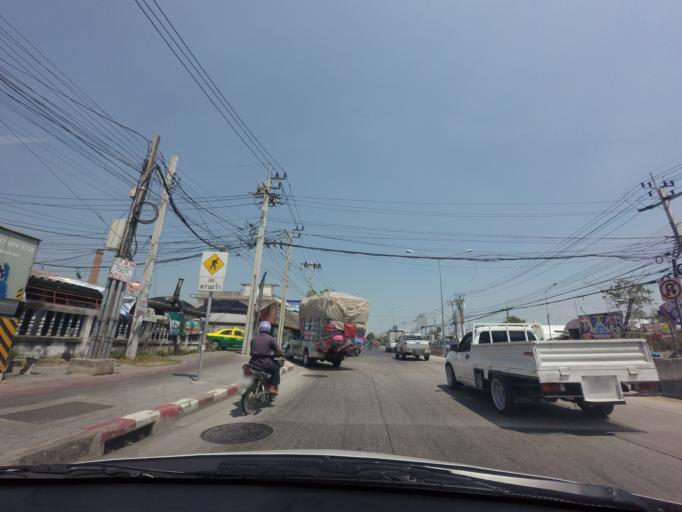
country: TH
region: Bangkok
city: Nong Chok
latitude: 13.8559
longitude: 100.8541
